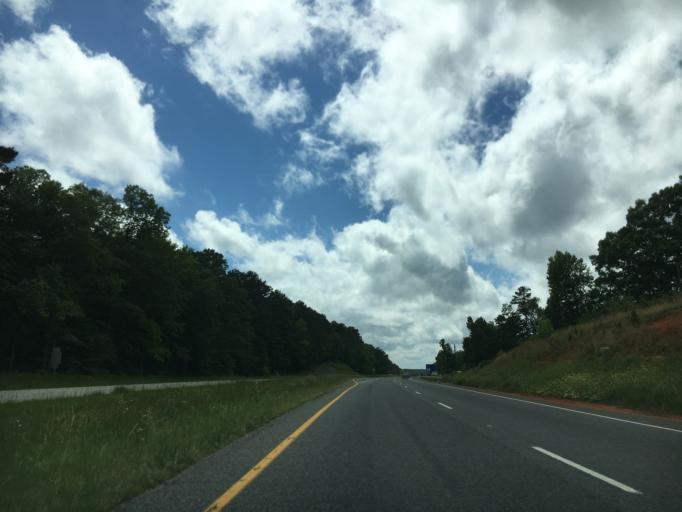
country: US
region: Virginia
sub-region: Mecklenburg County
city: Clarksville
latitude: 36.6378
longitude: -78.5223
